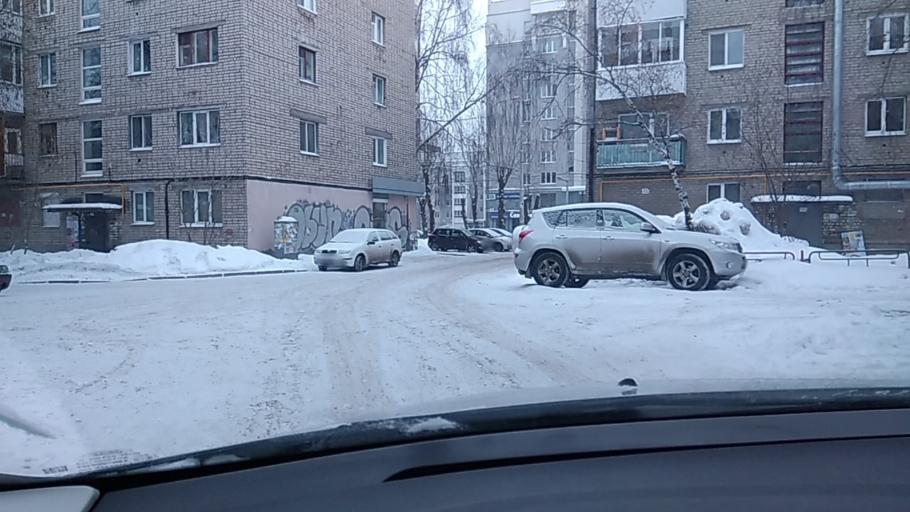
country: RU
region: Sverdlovsk
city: Yekaterinburg
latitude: 56.8099
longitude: 60.6172
